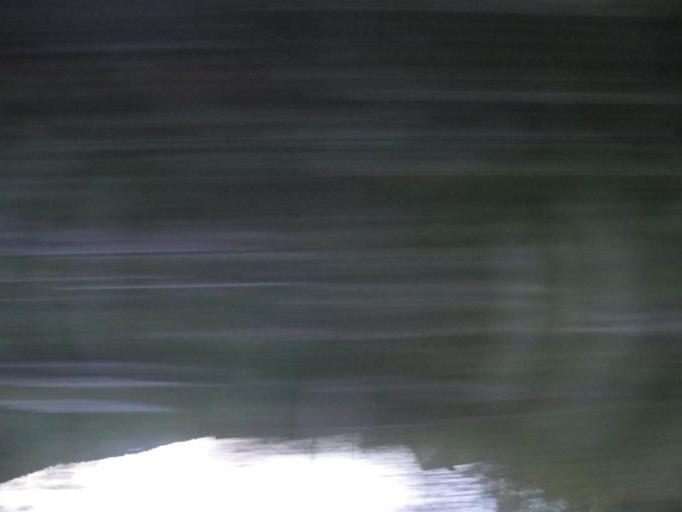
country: NO
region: Oppland
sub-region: Sor-Fron
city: Hundorp
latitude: 61.5466
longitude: 9.9649
